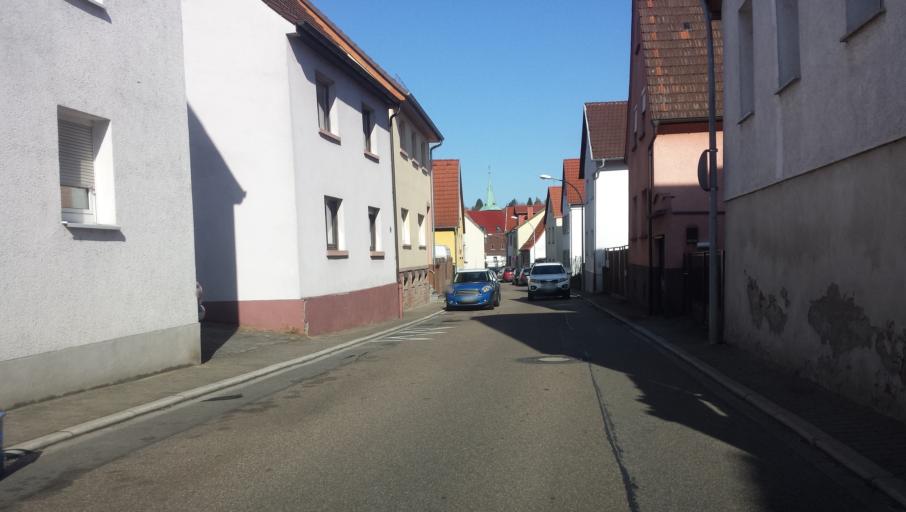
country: DE
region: Baden-Wuerttemberg
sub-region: Karlsruhe Region
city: Dielheim
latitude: 49.2806
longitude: 8.7333
